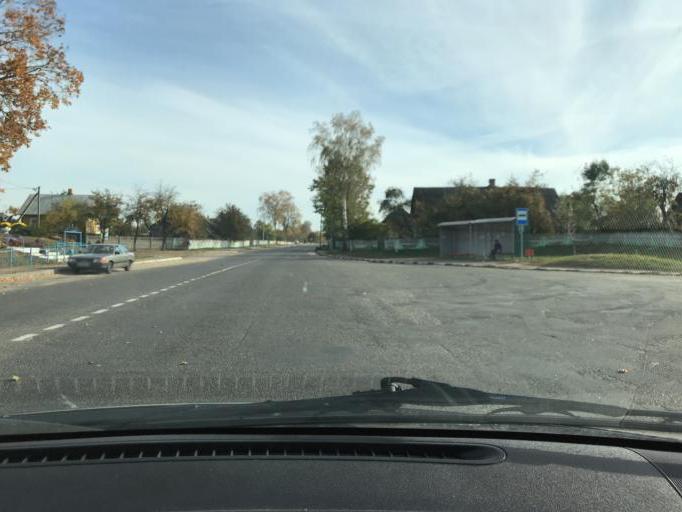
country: BY
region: Brest
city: Asnyezhytsy
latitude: 52.1966
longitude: 26.0685
